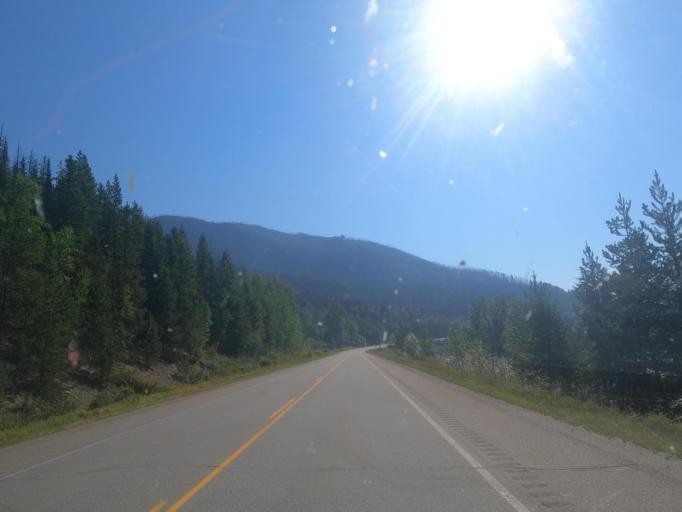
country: CA
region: Alberta
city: Jasper Park Lodge
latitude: 52.9528
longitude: -118.8718
